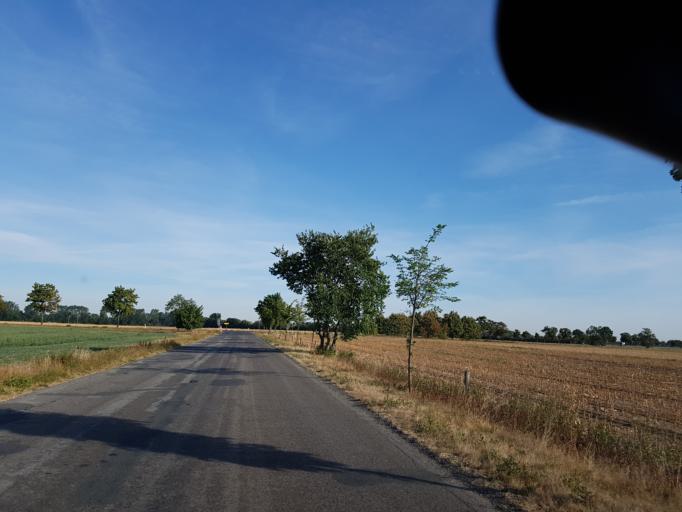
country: DE
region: Saxony
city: Nauwalde
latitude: 51.4514
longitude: 13.3878
